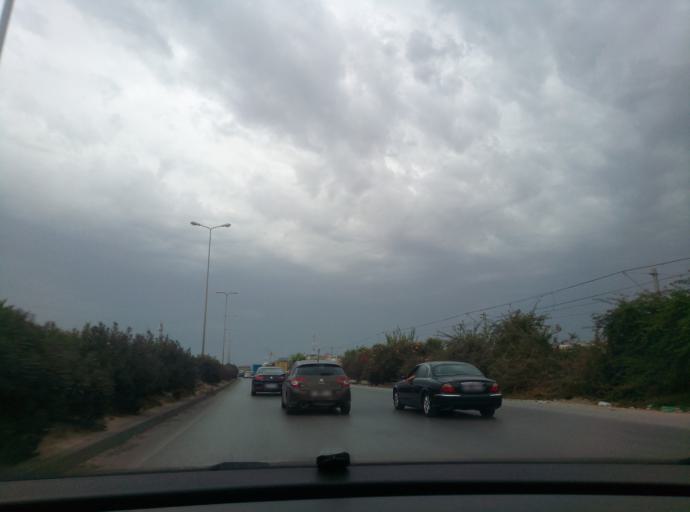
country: TN
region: Bin 'Arus
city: Ben Arous
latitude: 36.7541
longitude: 10.2028
